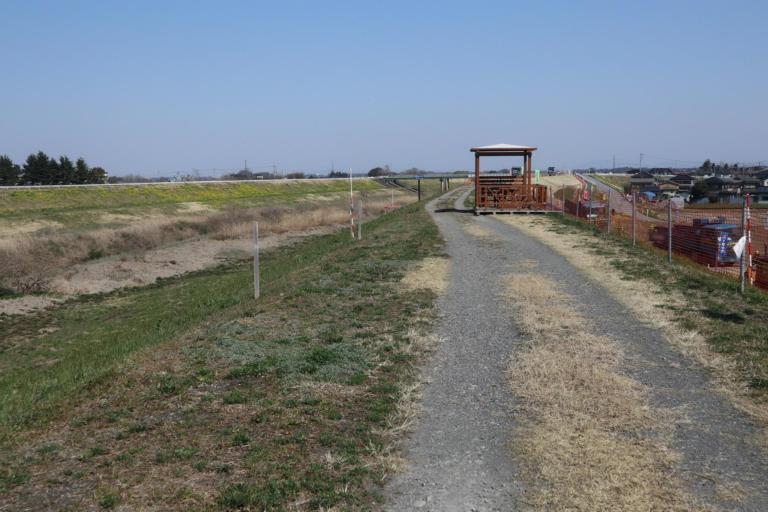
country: JP
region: Tochigi
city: Fujioka
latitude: 36.2707
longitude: 139.7082
